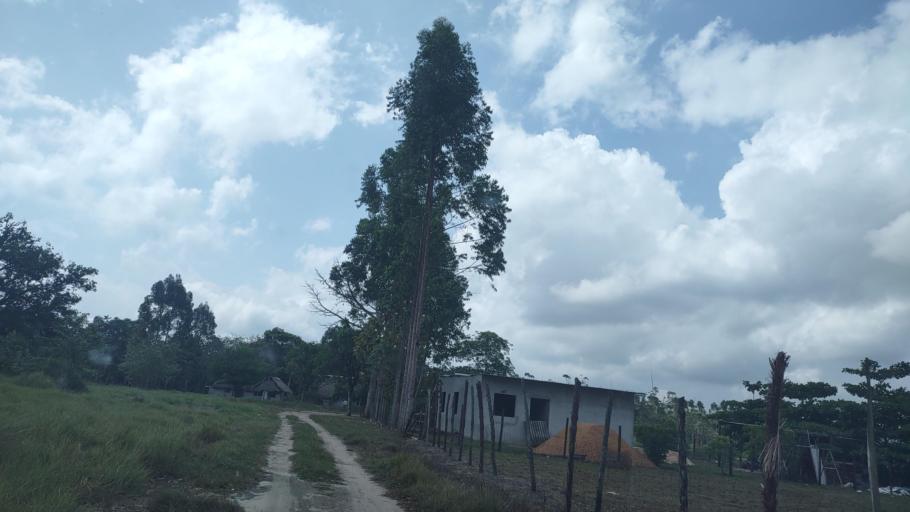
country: MX
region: Veracruz
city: Las Choapas
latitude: 17.9476
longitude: -94.0953
